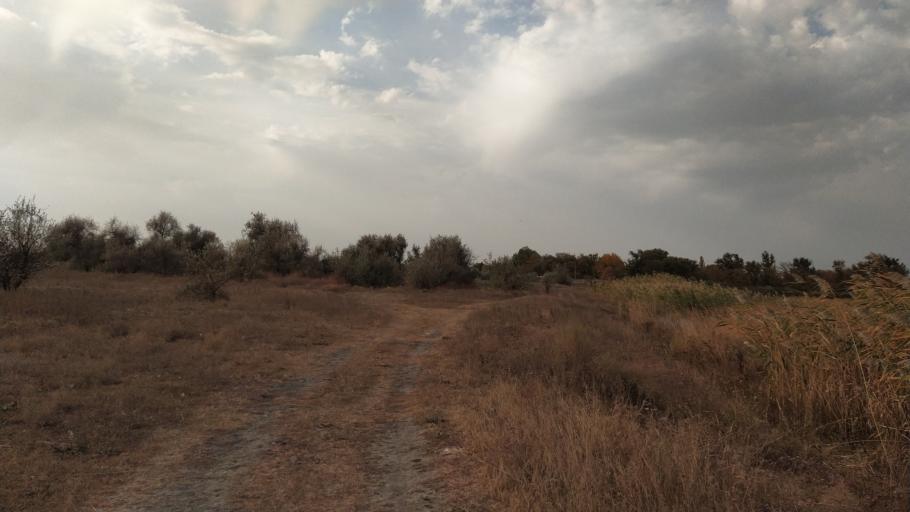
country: RU
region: Rostov
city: Kuleshovka
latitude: 47.1407
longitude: 39.5823
